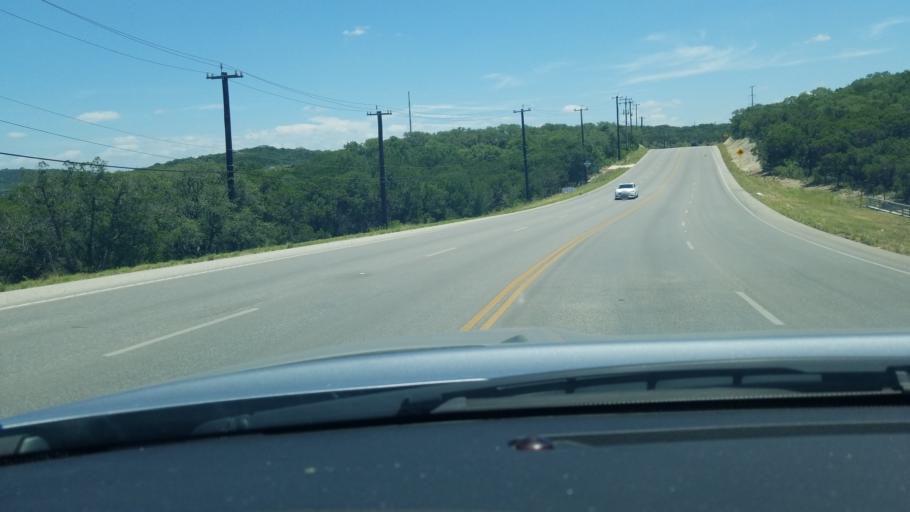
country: US
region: Texas
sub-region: Bexar County
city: Timberwood Park
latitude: 29.7135
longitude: -98.4520
